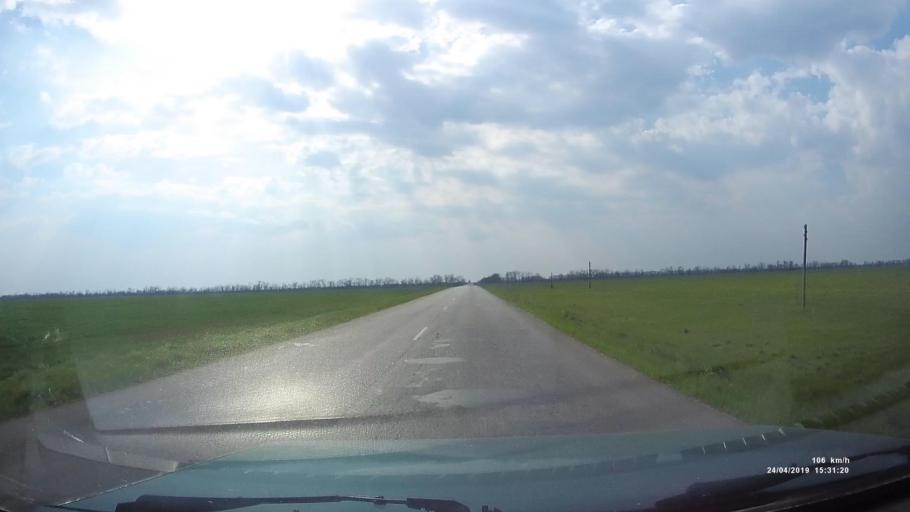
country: RU
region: Rostov
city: Remontnoye
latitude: 46.5996
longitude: 42.9856
